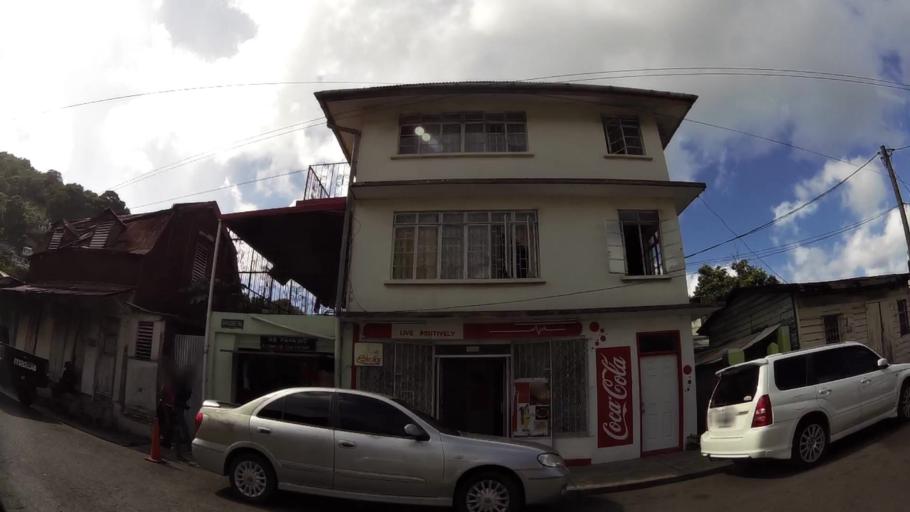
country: LC
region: Castries Quarter
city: Castries
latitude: 14.0069
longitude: -60.9882
